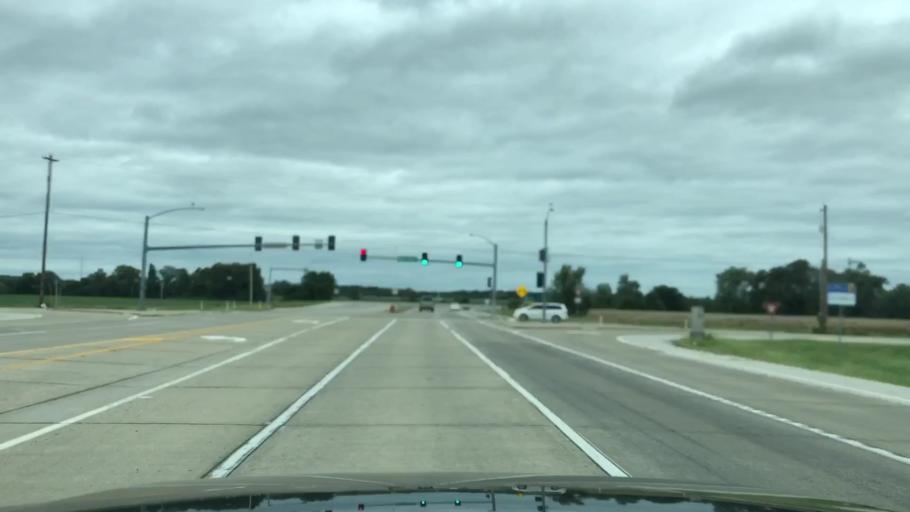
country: US
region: Missouri
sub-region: Saint Louis County
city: Maryland Heights
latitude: 38.7168
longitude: -90.4991
